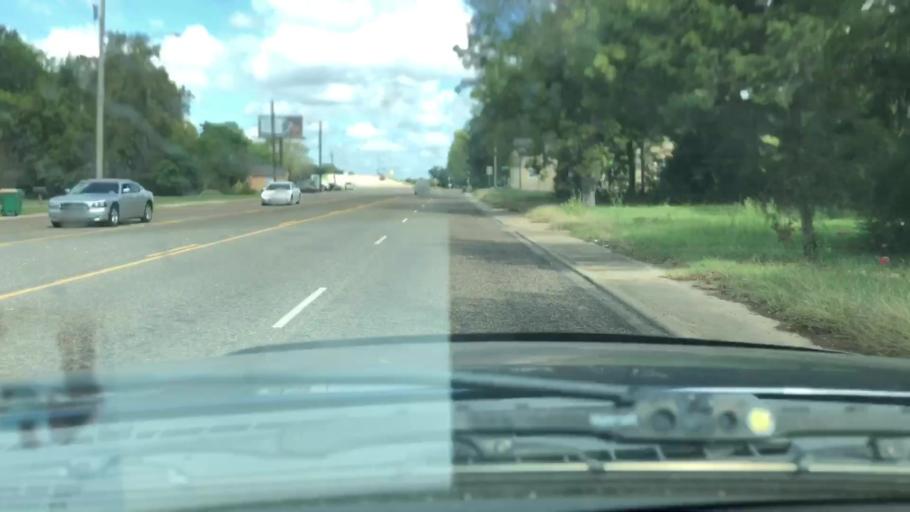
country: US
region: Texas
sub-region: Bowie County
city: Texarkana
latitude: 33.4092
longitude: -94.0605
